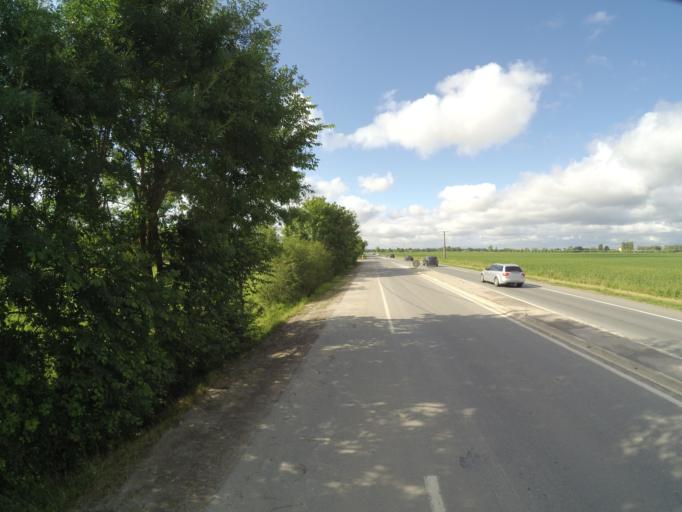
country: FR
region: Aquitaine
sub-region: Departement de la Gironde
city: Saint-Louis-de-Montferrand
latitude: 44.9165
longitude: -0.5622
